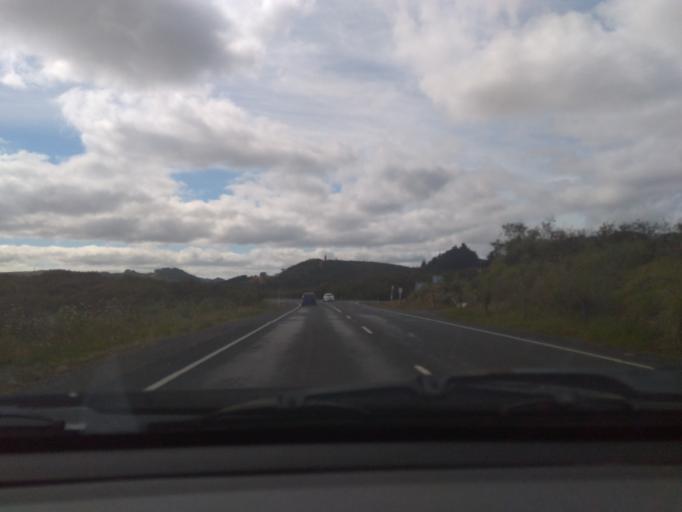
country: NZ
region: Northland
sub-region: Far North District
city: Taipa
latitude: -35.0102
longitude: 173.5422
